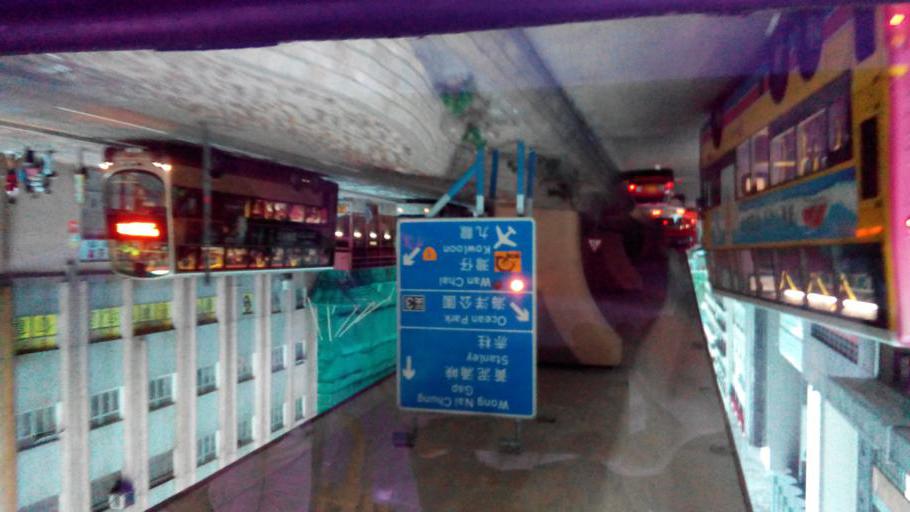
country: HK
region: Wanchai
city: Wan Chai
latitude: 22.2495
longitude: 114.1677
